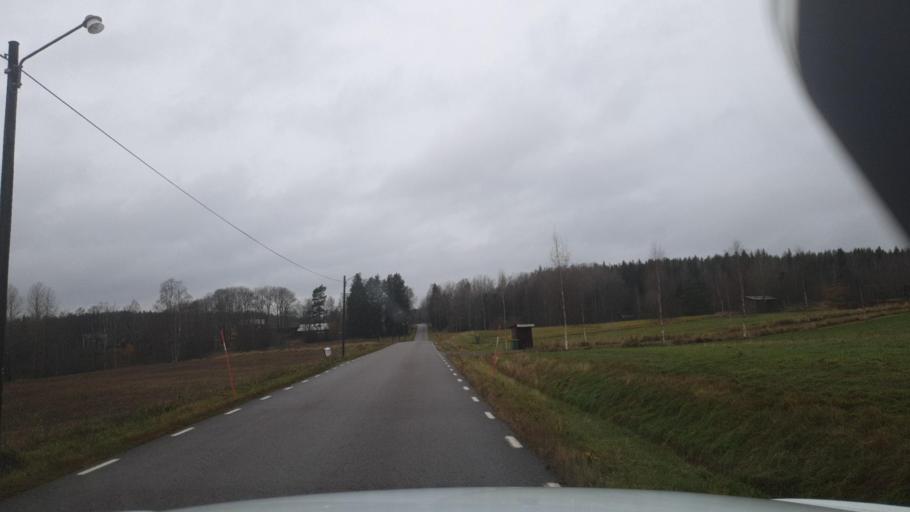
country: SE
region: Vaermland
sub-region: Arvika Kommun
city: Arvika
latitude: 59.5709
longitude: 12.5096
